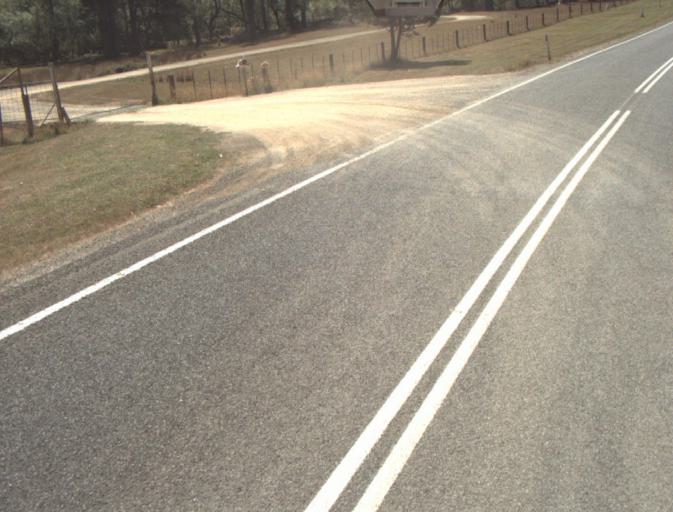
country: AU
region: Tasmania
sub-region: Dorset
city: Scottsdale
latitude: -41.3018
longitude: 147.3818
